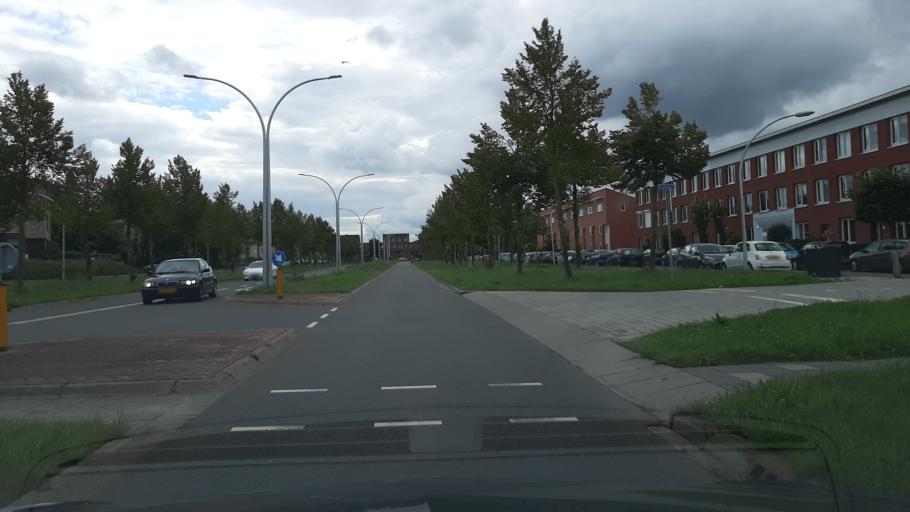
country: NL
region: Overijssel
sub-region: Gemeente Zwolle
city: Zwolle
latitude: 52.5407
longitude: 6.0533
